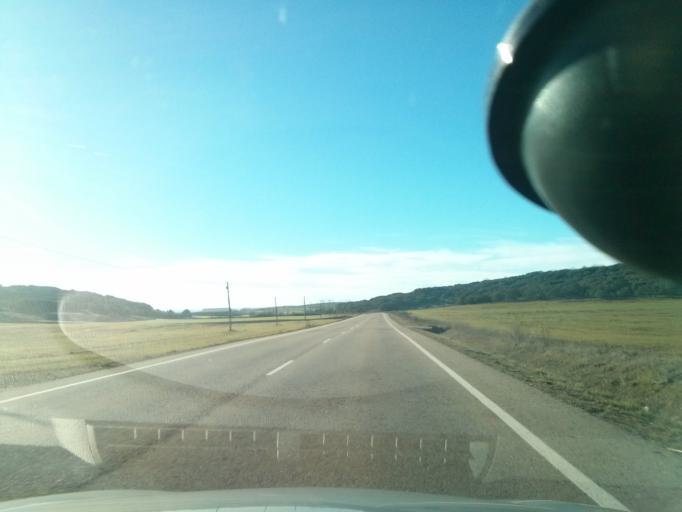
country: ES
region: Castille and Leon
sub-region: Provincia de Burgos
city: Abajas
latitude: 42.6181
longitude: -3.6315
